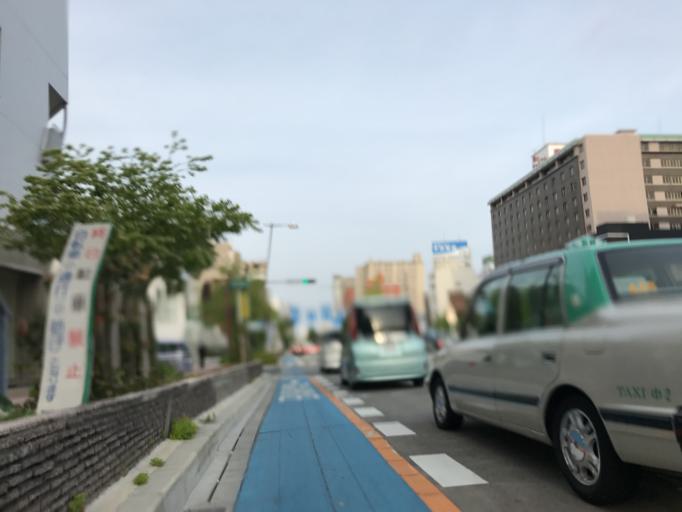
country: JP
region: Aichi
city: Nagoya-shi
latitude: 35.1743
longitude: 136.9170
